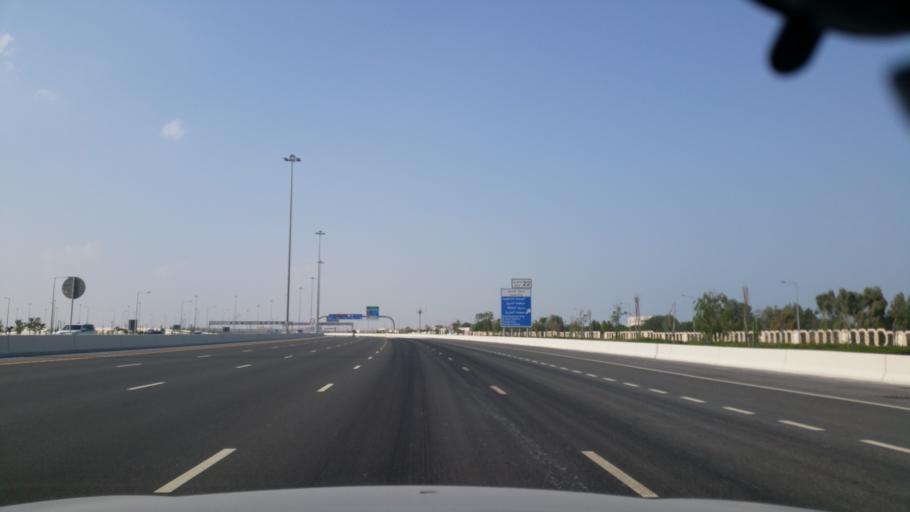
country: QA
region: Baladiyat Umm Salal
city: Umm Salal Muhammad
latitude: 25.3844
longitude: 51.5004
